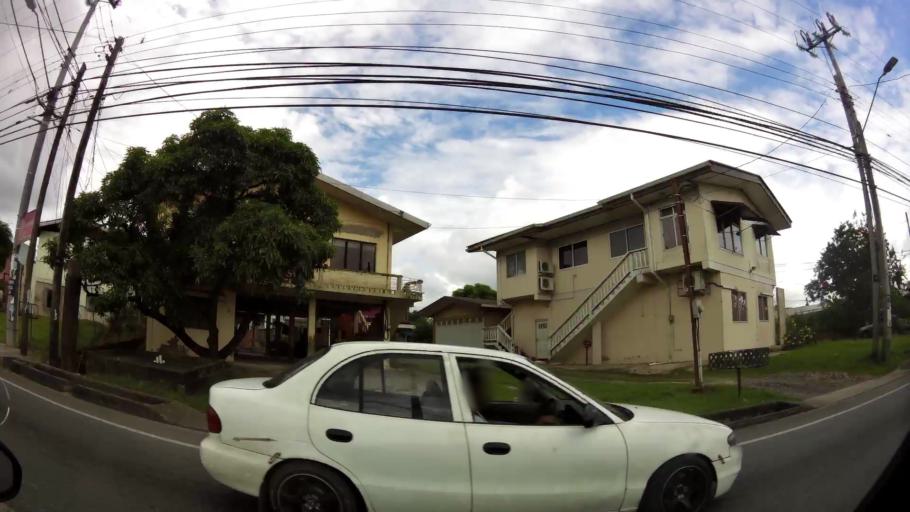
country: TT
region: Chaguanas
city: Chaguanas
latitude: 10.4778
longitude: -61.4106
